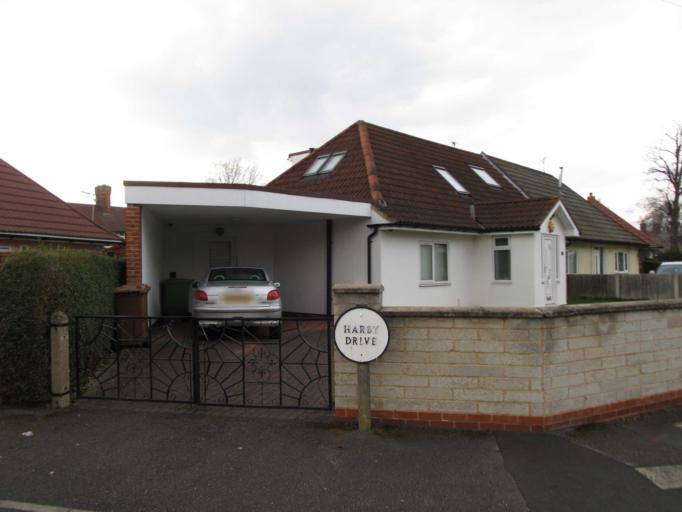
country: GB
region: England
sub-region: Nottingham
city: Nottingham
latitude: 52.9524
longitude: -1.1892
